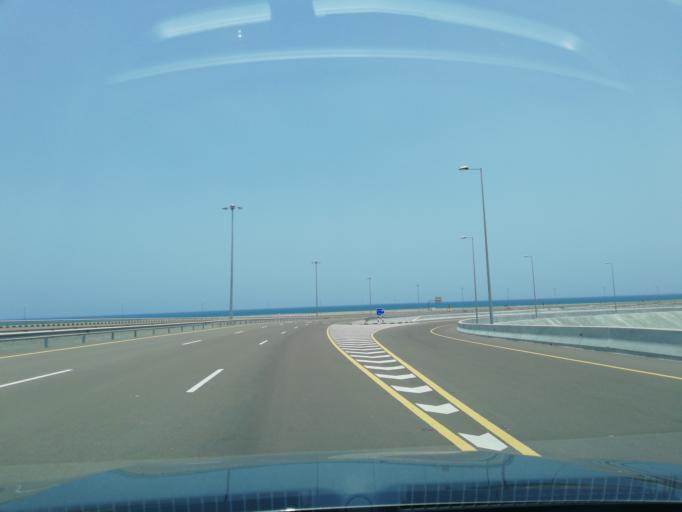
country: AE
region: Al Fujayrah
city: Al Fujayrah
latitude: 24.9533
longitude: 56.3732
